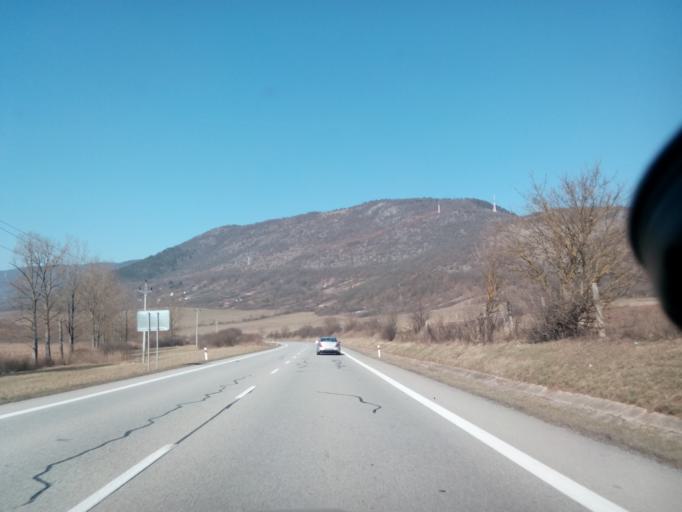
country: SK
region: Kosicky
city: Medzev
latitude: 48.6081
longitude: 20.8674
